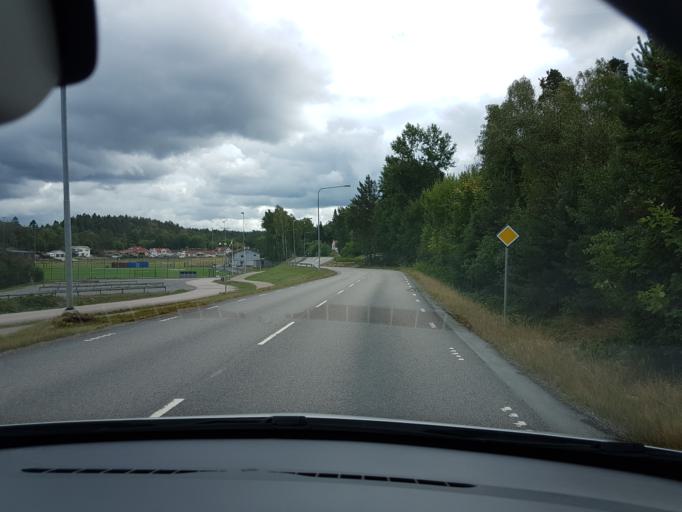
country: SE
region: Vaestra Goetaland
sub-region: Ale Kommun
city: Nodinge-Nol
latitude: 57.8876
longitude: 12.0755
